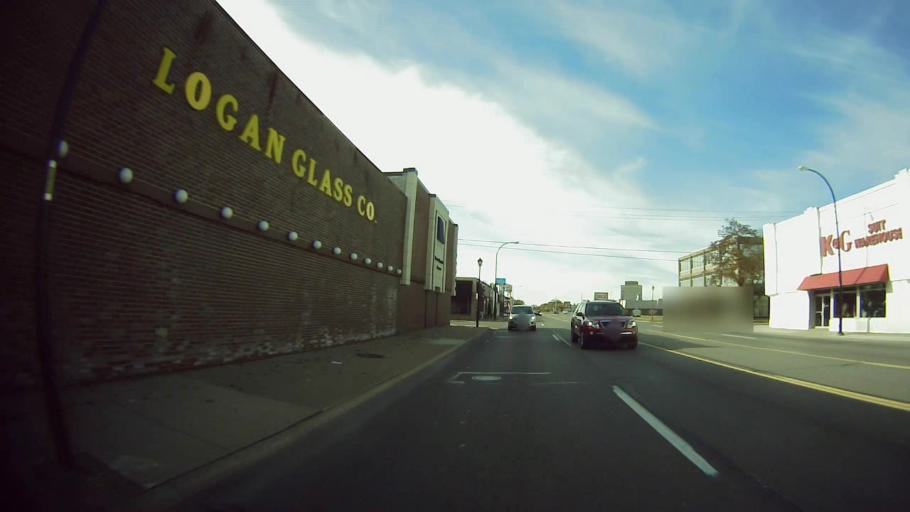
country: US
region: Michigan
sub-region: Wayne County
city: Dearborn Heights
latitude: 42.3037
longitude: -83.2548
